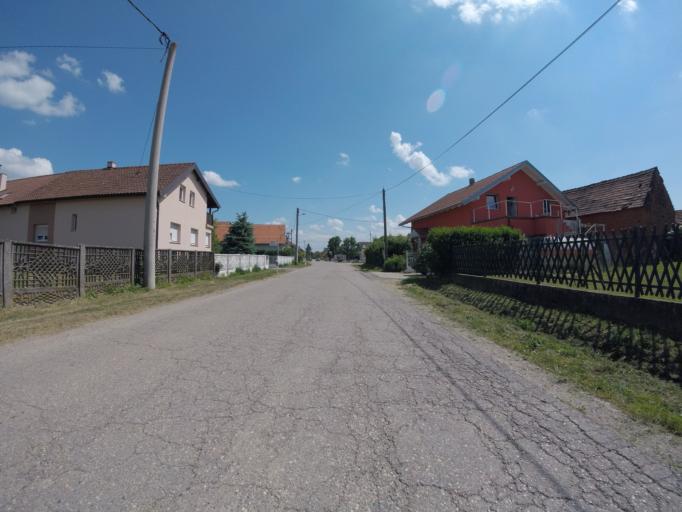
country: HR
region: Zagrebacka
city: Mraclin
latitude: 45.6758
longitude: 16.0685
